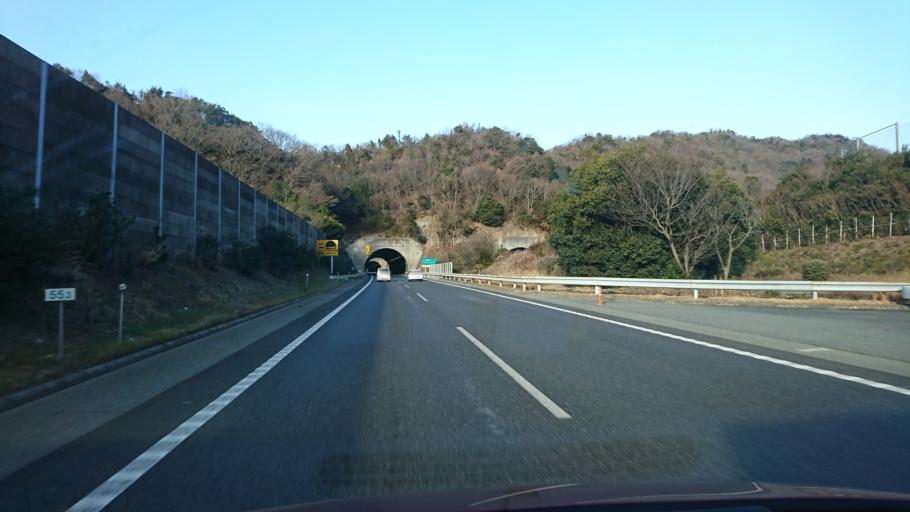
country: JP
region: Hyogo
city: Himeji
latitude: 34.8747
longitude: 134.6888
